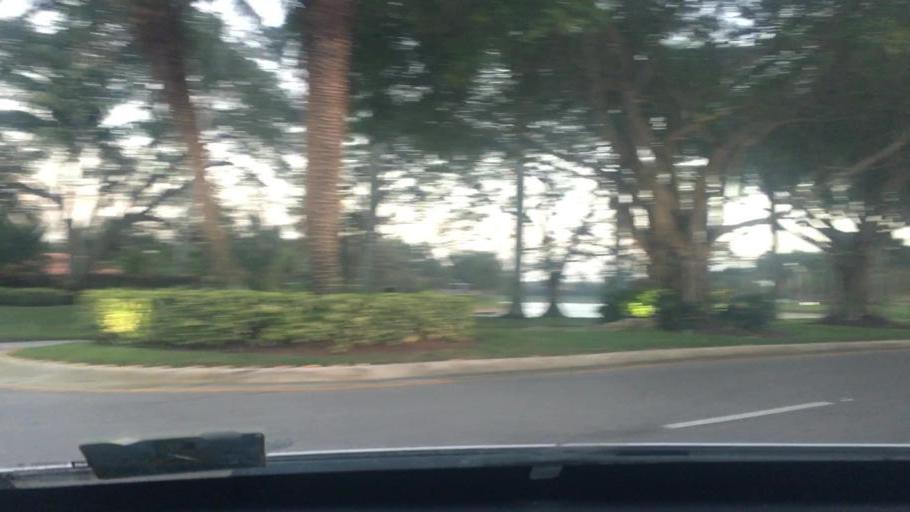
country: US
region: Florida
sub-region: Palm Beach County
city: Plantation Mobile Home Park
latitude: 26.7129
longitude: -80.1592
